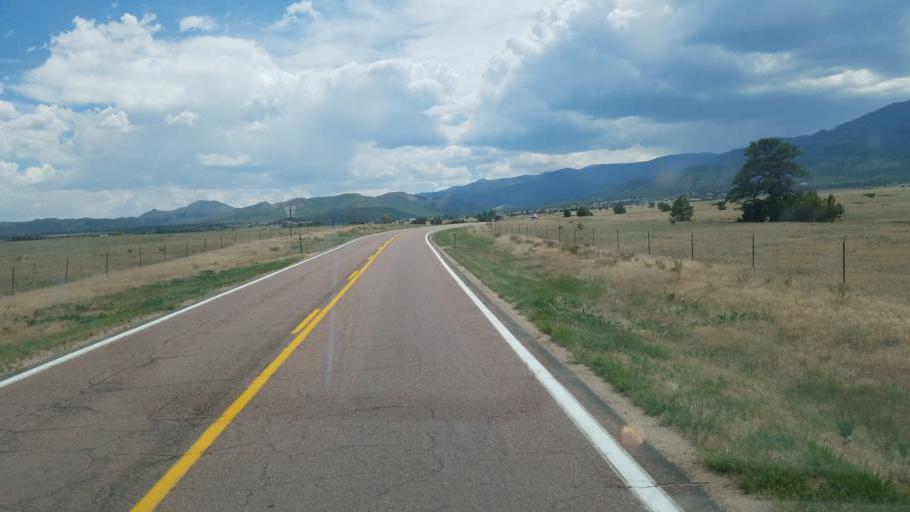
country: US
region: Colorado
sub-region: Fremont County
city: Florence
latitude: 38.2631
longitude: -105.0875
